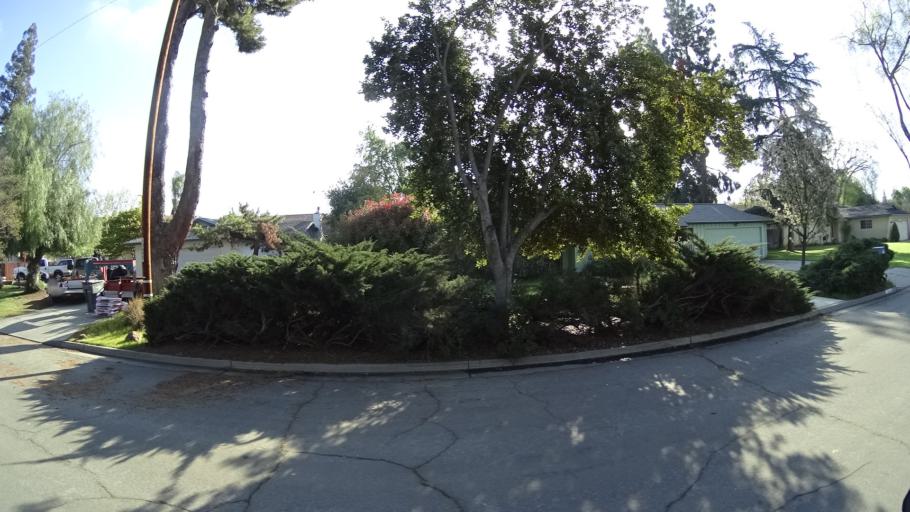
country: US
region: California
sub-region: Fresno County
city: Fresno
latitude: 36.8206
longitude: -119.8281
